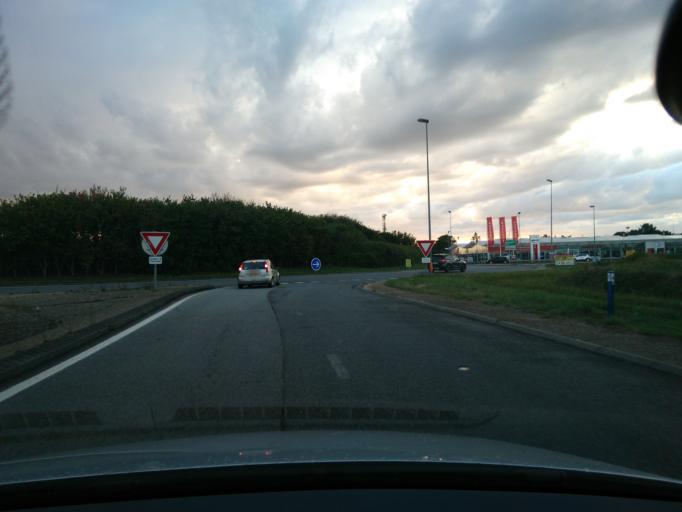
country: FR
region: Haute-Normandie
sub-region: Departement de l'Eure
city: Evreux
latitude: 48.9996
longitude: 1.1556
